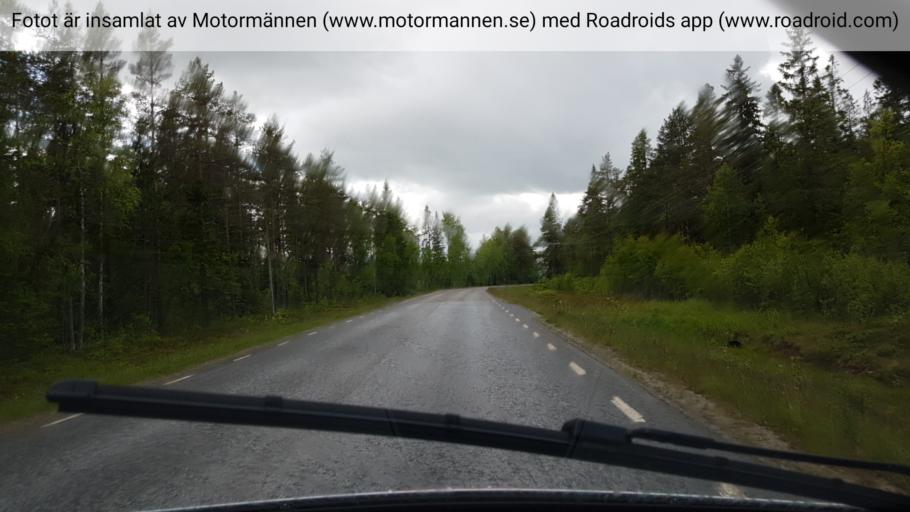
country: SE
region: Vaesterbotten
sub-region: Vannas Kommun
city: Vannasby
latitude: 63.8510
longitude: 19.9398
